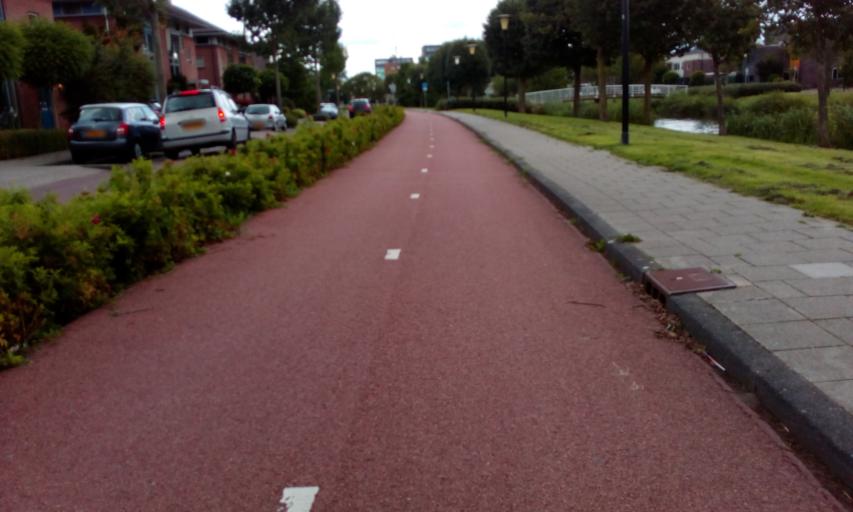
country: NL
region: South Holland
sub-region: Gemeente Binnenmaas
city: Heinenoord
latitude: 51.8524
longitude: 4.4968
